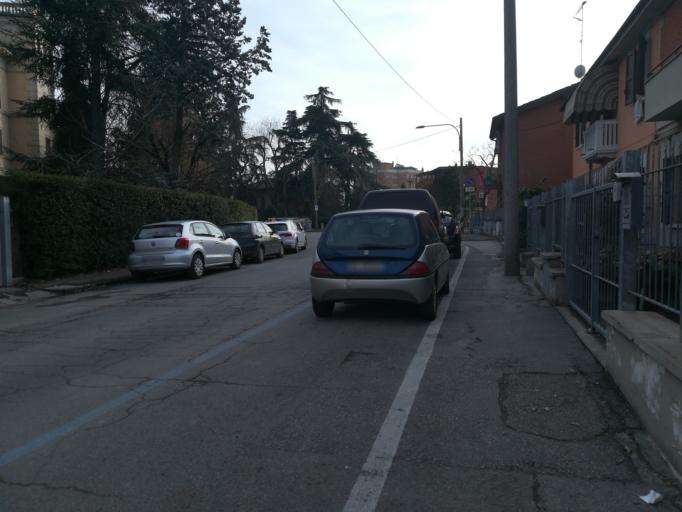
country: IT
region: Emilia-Romagna
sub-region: Provincia di Bologna
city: Progresso
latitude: 44.5455
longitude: 11.3536
